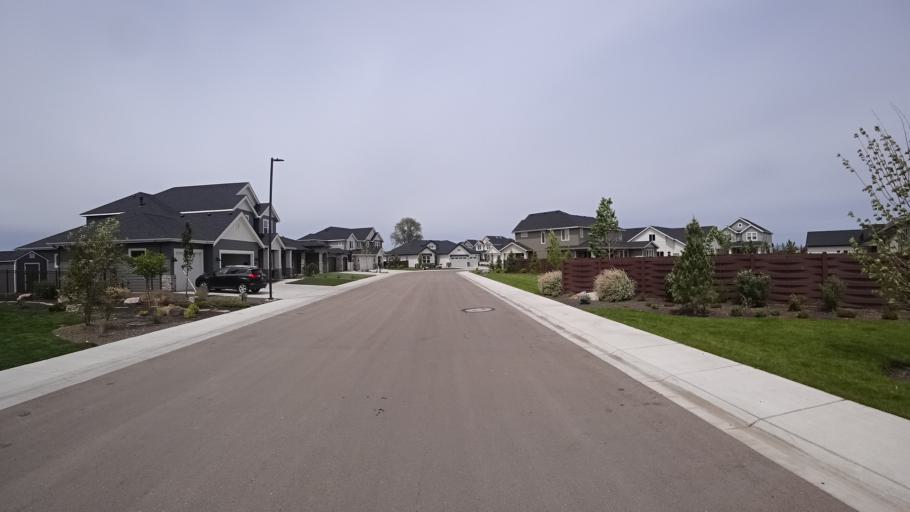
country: US
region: Idaho
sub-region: Ada County
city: Meridian
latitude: 43.5564
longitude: -116.3404
